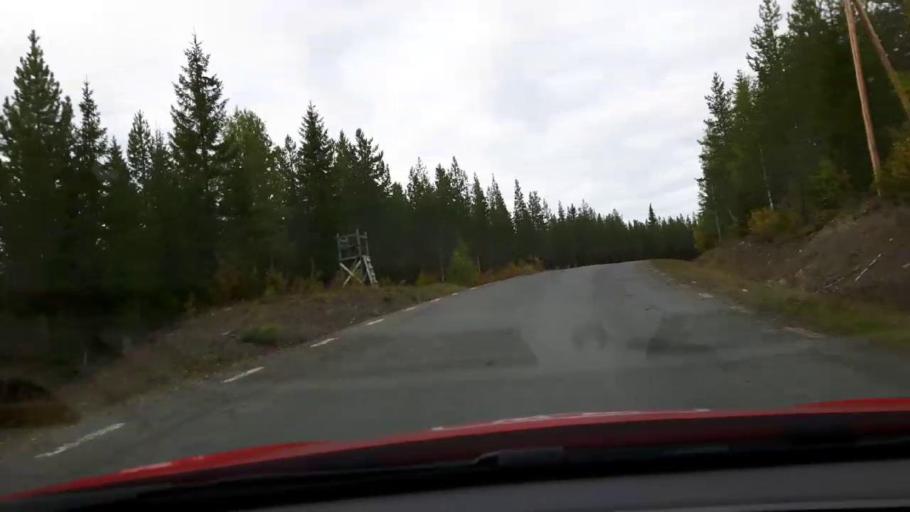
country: SE
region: Jaemtland
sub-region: Krokoms Kommun
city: Krokom
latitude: 63.2117
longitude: 14.1170
